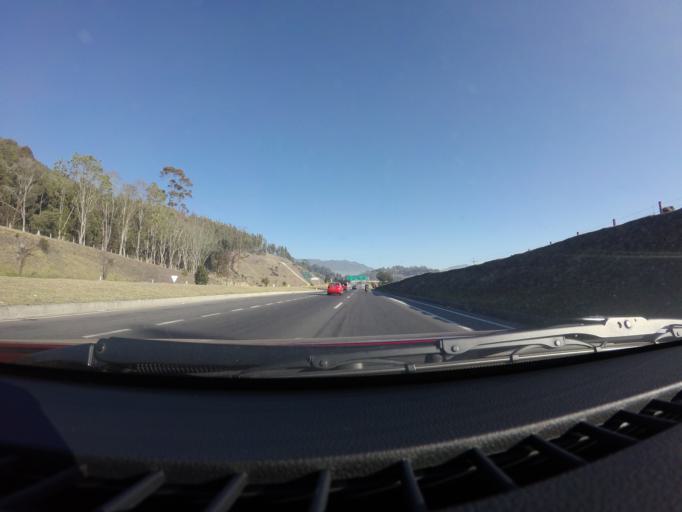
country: CO
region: Cundinamarca
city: Zipaquira
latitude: 4.9926
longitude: -74.0035
